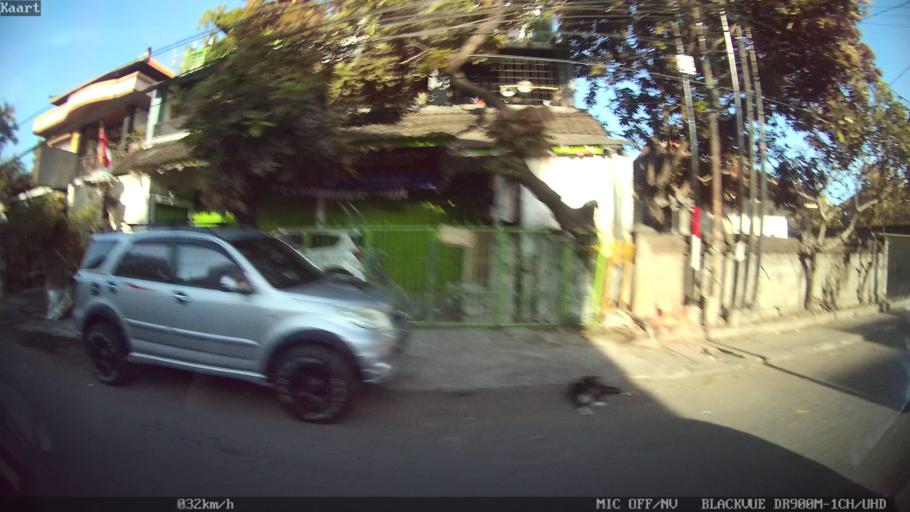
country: ID
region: Bali
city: Denpasar
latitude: -8.6408
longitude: 115.2221
